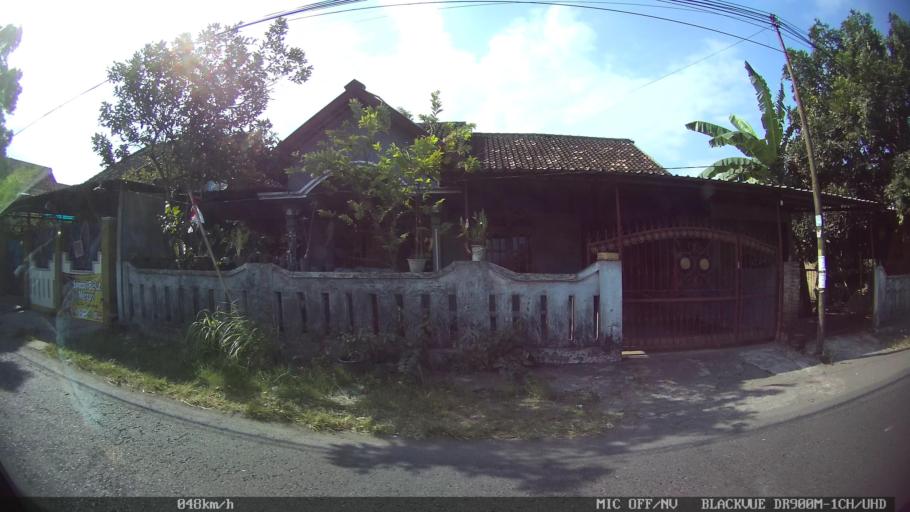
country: ID
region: Daerah Istimewa Yogyakarta
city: Sewon
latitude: -7.8734
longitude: 110.3717
